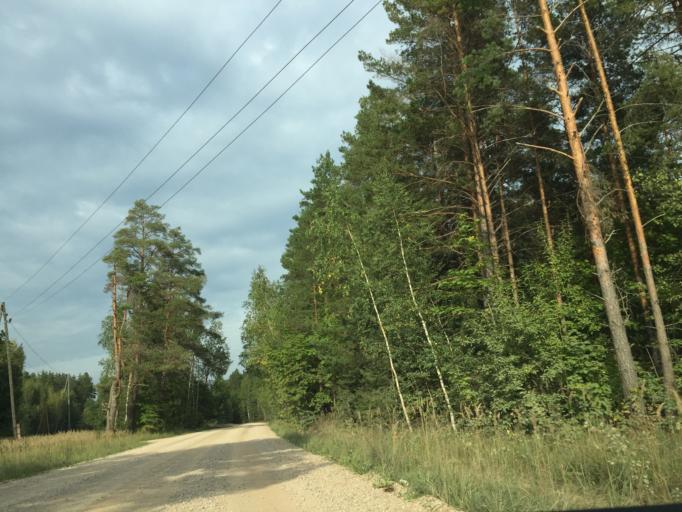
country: LV
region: Ikskile
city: Ikskile
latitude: 56.8068
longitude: 24.4417
